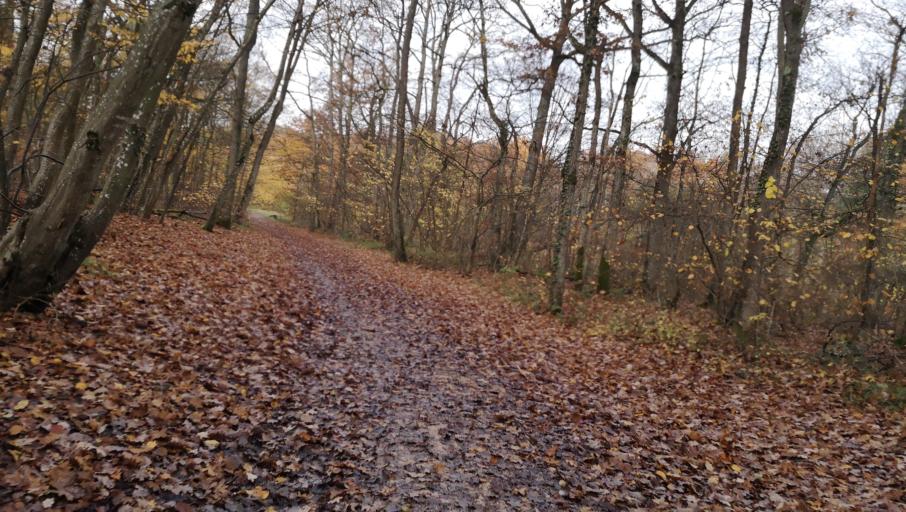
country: FR
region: Centre
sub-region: Departement du Loiret
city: Semoy
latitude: 47.9422
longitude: 1.9650
